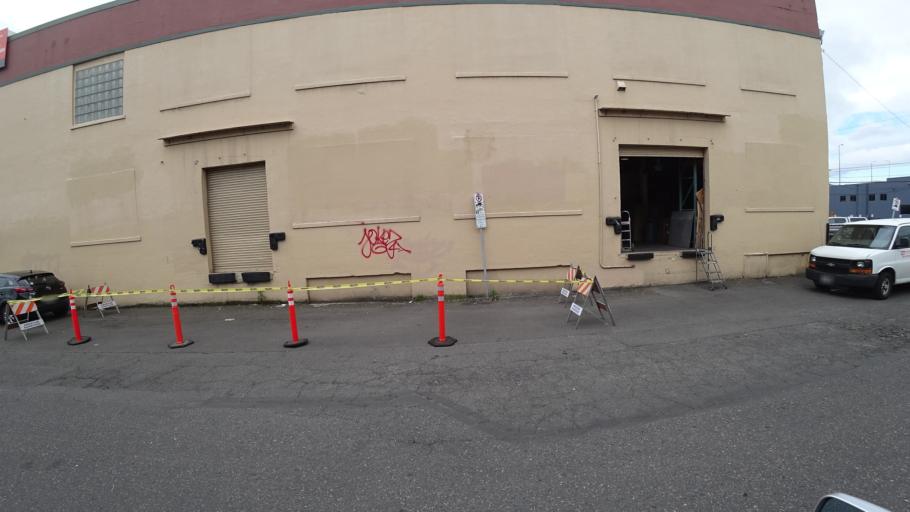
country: US
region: Oregon
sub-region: Multnomah County
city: Portland
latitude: 45.5154
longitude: -122.6638
